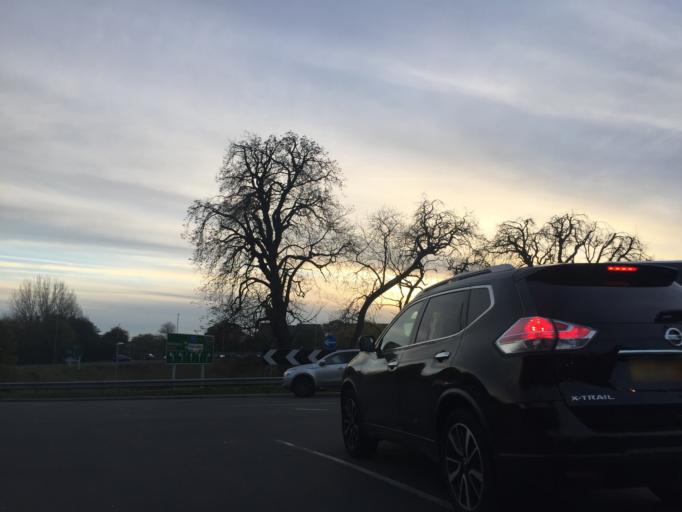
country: GB
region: England
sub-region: Northamptonshire
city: Northampton
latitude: 52.2770
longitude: -0.8446
